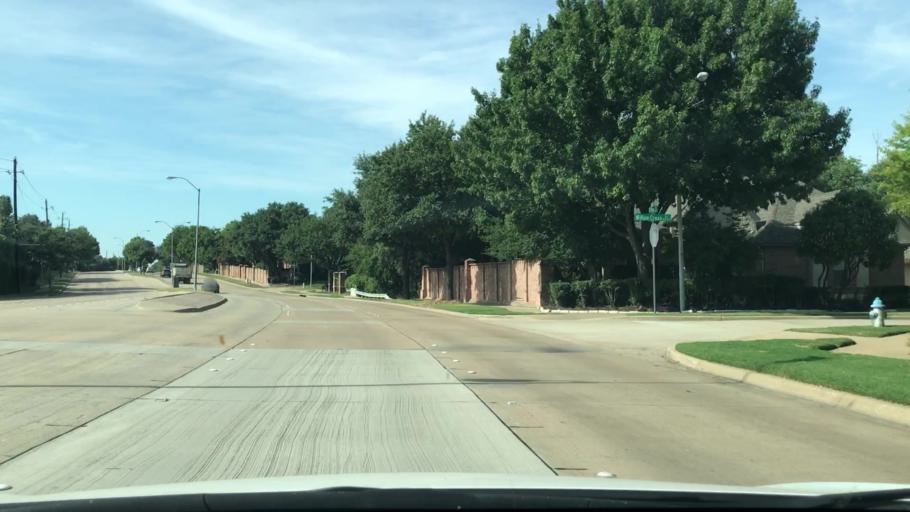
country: US
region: Texas
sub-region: Denton County
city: The Colony
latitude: 33.0524
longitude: -96.8392
